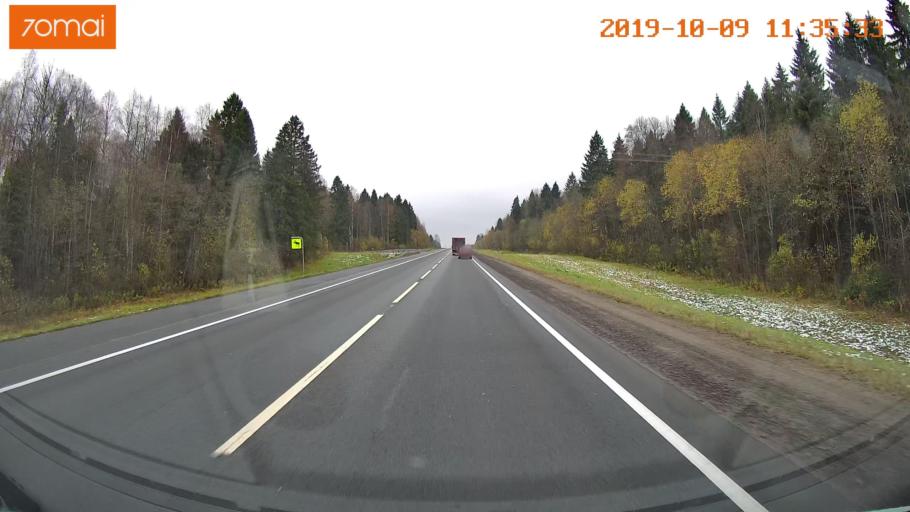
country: RU
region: Vologda
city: Gryazovets
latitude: 59.0018
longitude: 40.1273
